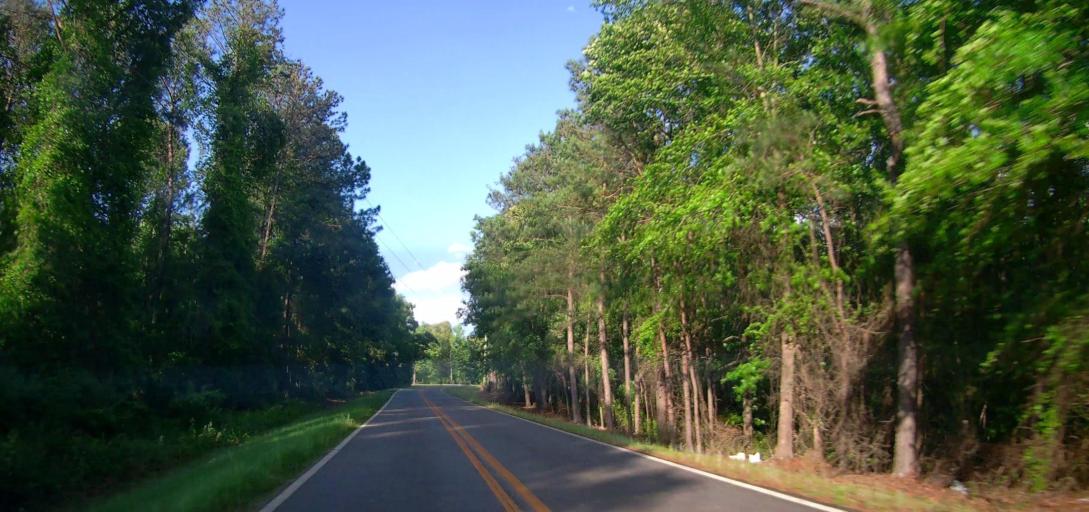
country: US
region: Georgia
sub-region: Peach County
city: Byron
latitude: 32.6717
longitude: -83.7993
